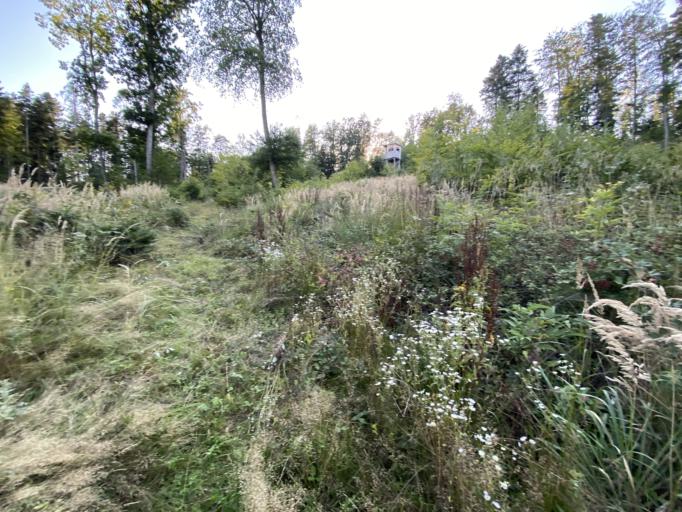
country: AT
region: Burgenland
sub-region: Politischer Bezirk Oberpullendorf
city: Kobersdorf
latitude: 47.5831
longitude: 16.3771
